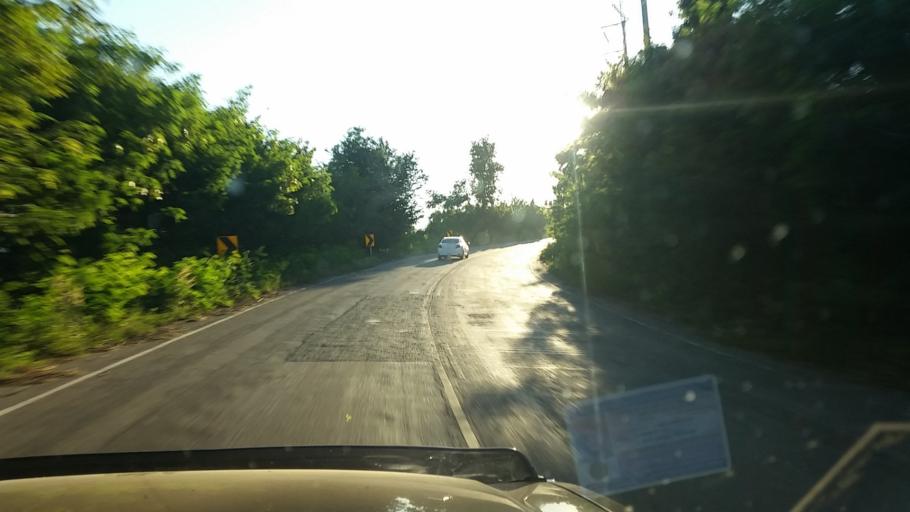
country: TH
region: Chaiyaphum
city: Nong Bua Rawe
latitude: 15.6838
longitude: 101.7013
